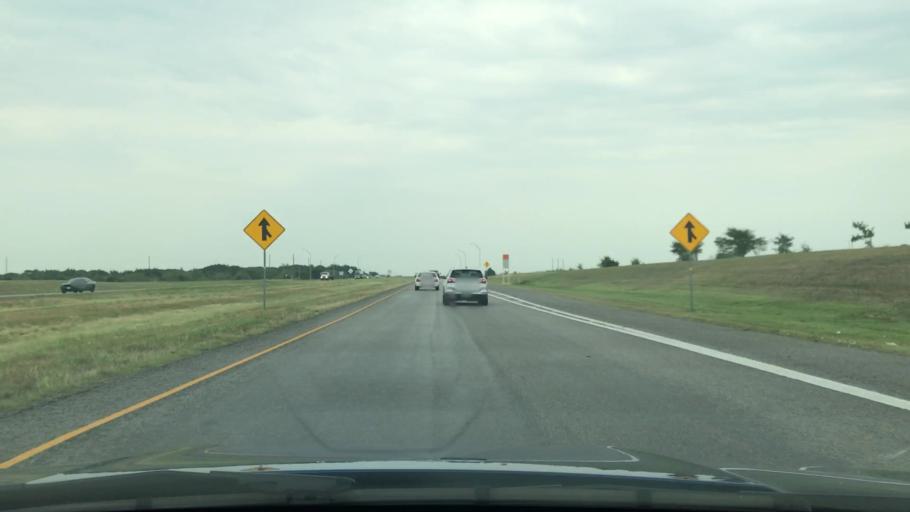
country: US
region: Texas
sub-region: Kaufman County
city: Terrell
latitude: 32.7205
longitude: -96.3193
